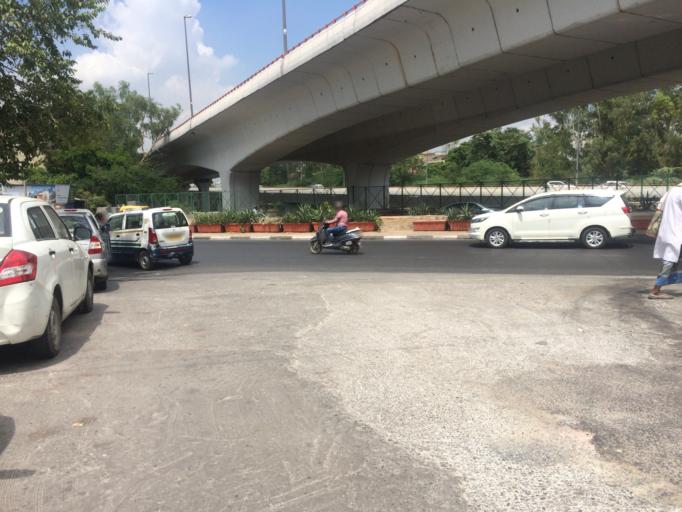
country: IN
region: NCT
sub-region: New Delhi
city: New Delhi
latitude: 28.5855
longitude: 77.2406
